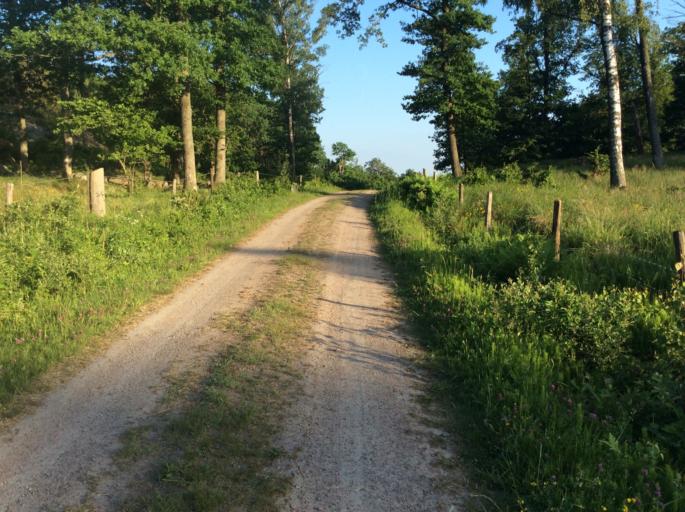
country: SE
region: Vaestra Goetaland
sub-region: Goteborg
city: Torslanda
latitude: 57.7950
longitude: 11.8579
